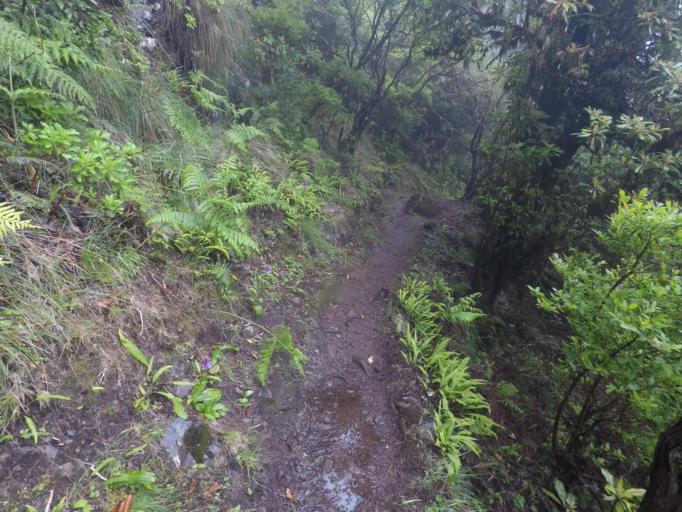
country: PT
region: Madeira
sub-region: Calheta
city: Arco da Calheta
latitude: 32.7741
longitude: -17.1219
